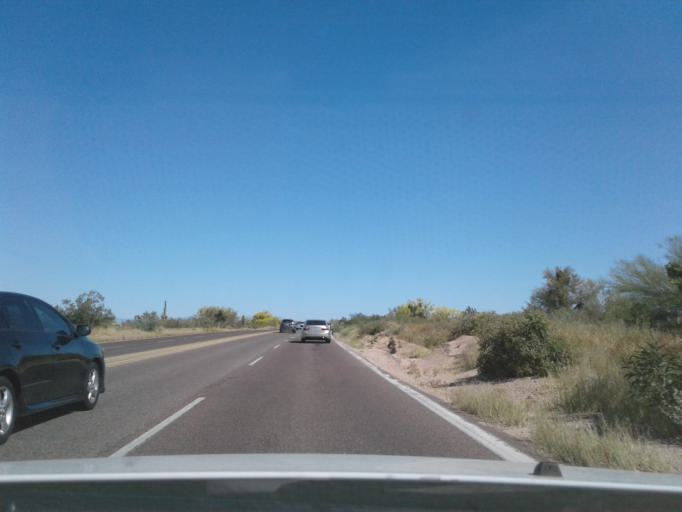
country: US
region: Arizona
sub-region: Maricopa County
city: Cave Creek
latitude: 33.7131
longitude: -111.9752
